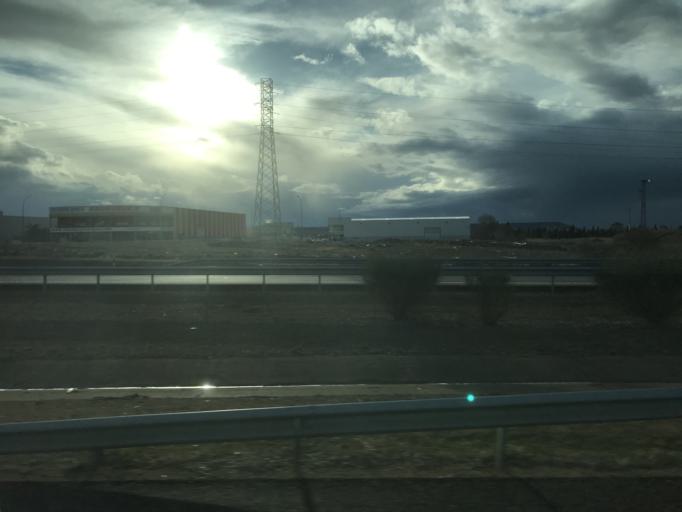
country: ES
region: Castille and Leon
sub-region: Provincia de Palencia
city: Villalobon
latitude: 42.0079
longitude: -4.5009
